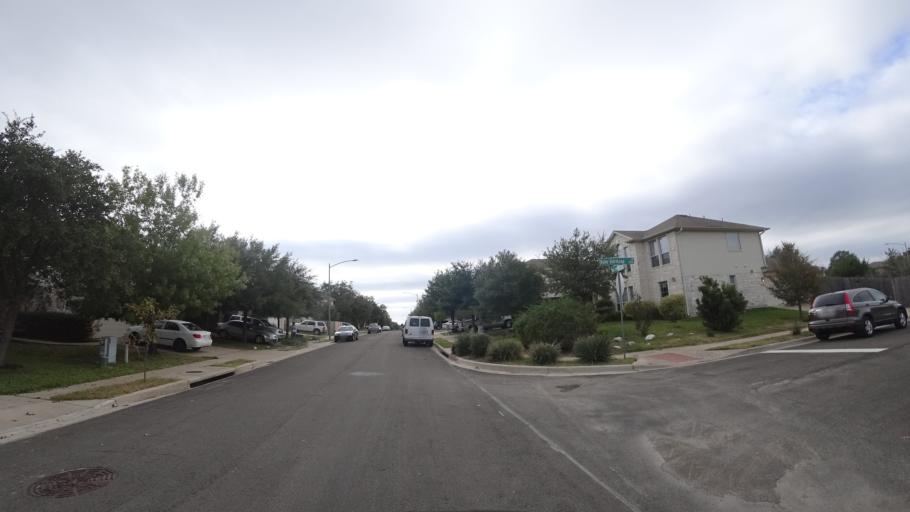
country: US
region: Texas
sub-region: Travis County
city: Manchaca
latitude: 30.1549
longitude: -97.8455
